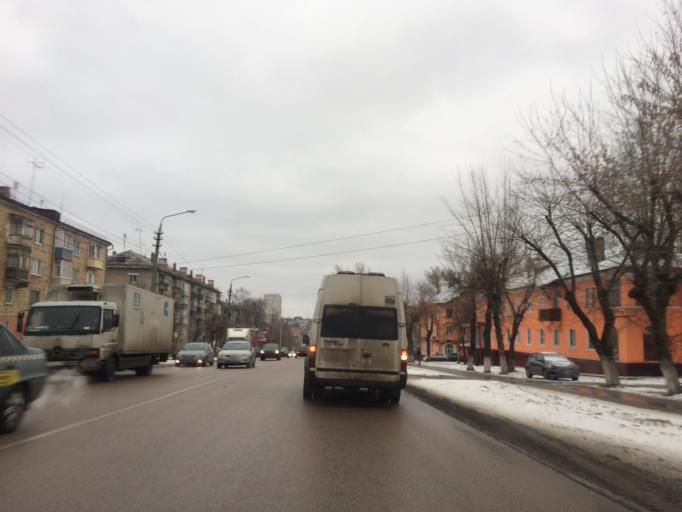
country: RU
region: Tula
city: Tula
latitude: 54.2079
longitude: 37.6730
